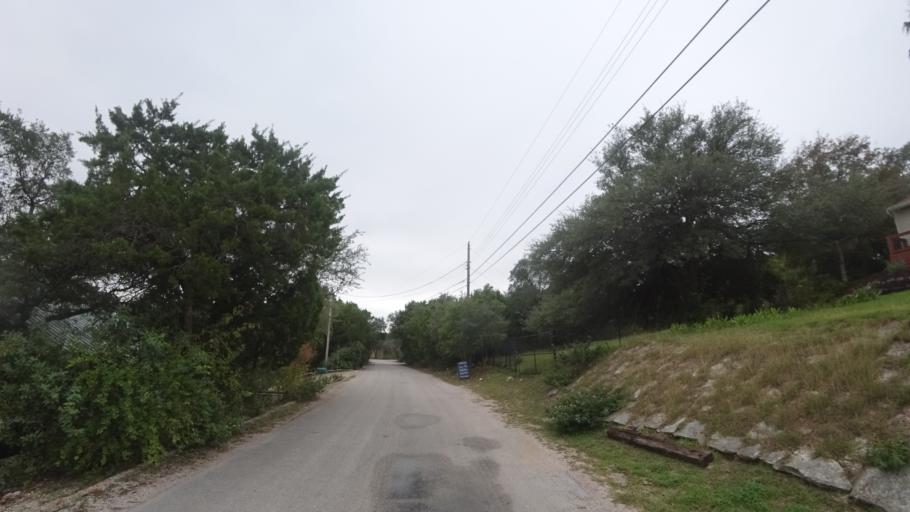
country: US
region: Texas
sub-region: Travis County
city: Hudson Bend
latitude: 30.3956
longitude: -97.9191
